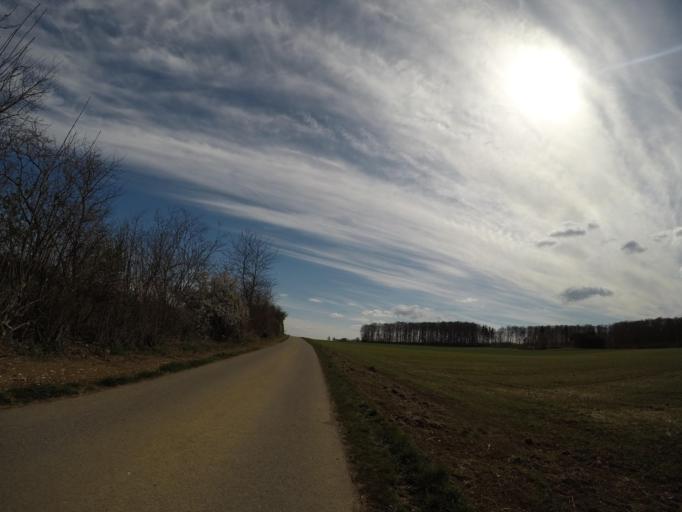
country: DE
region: Baden-Wuerttemberg
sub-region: Tuebingen Region
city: Mehrstetten
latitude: 48.3460
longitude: 9.5972
